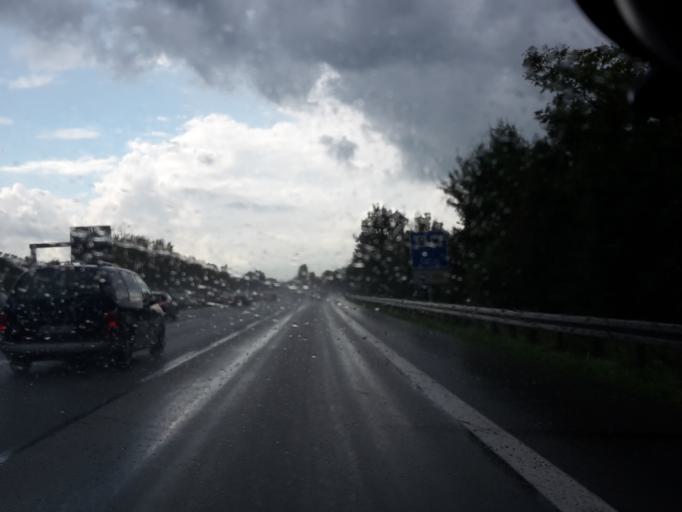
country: DE
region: Hesse
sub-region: Regierungsbezirk Darmstadt
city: Hochheim am Main
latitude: 50.0560
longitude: 8.3231
